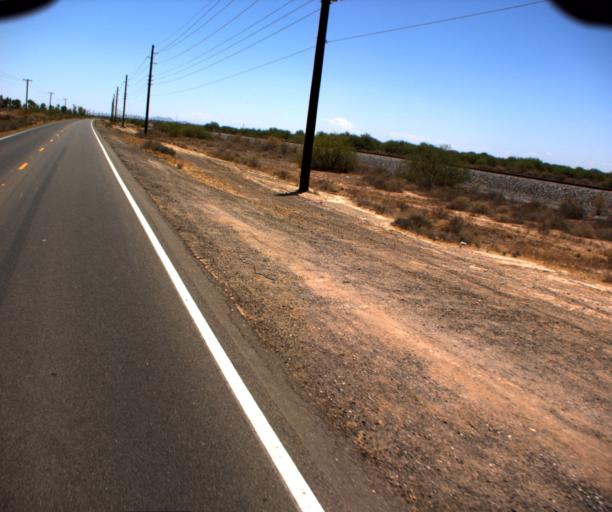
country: US
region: Arizona
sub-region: Pinal County
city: Maricopa
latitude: 33.0774
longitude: -112.0970
